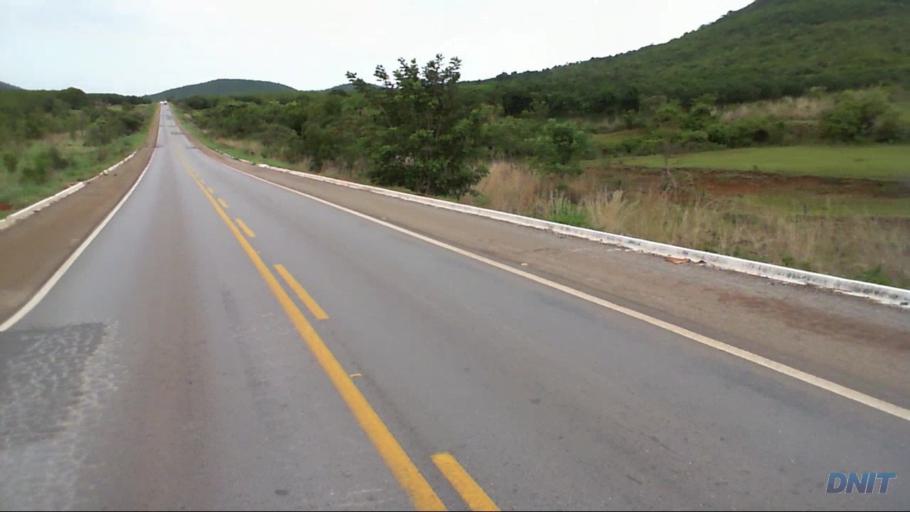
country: BR
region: Goias
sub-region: Barro Alto
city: Barro Alto
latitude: -14.9155
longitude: -48.9537
